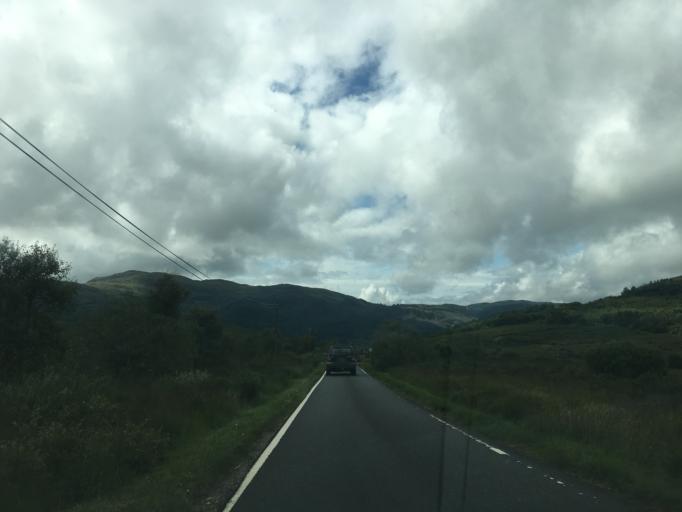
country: GB
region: Scotland
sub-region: Argyll and Bute
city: Port Bannatyne
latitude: 55.9880
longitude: -5.1608
